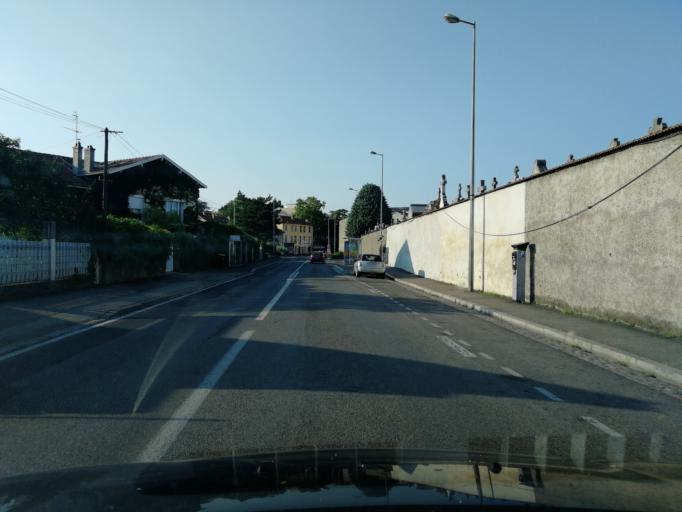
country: FR
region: Rhone-Alpes
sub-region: Departement du Rhone
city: Caluire-et-Cuire
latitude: 45.8015
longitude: 4.8513
